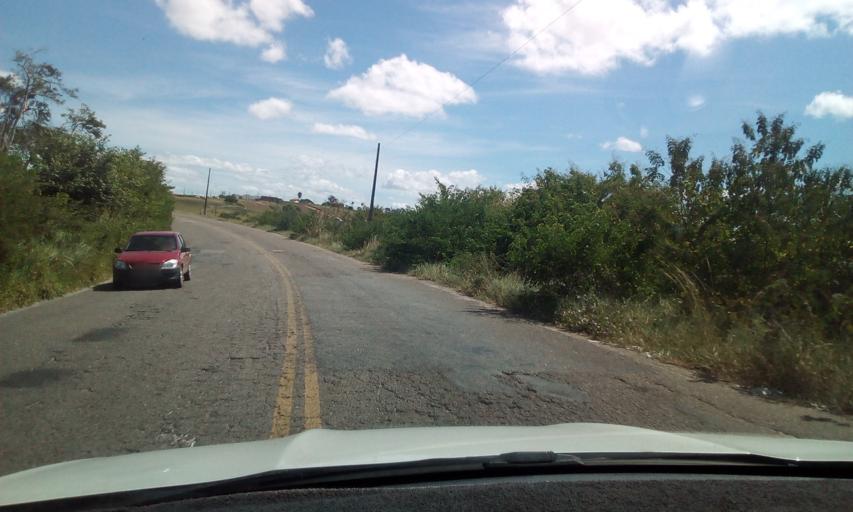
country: BR
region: Paraiba
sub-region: Areia
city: Remigio
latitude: -6.9578
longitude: -35.7838
